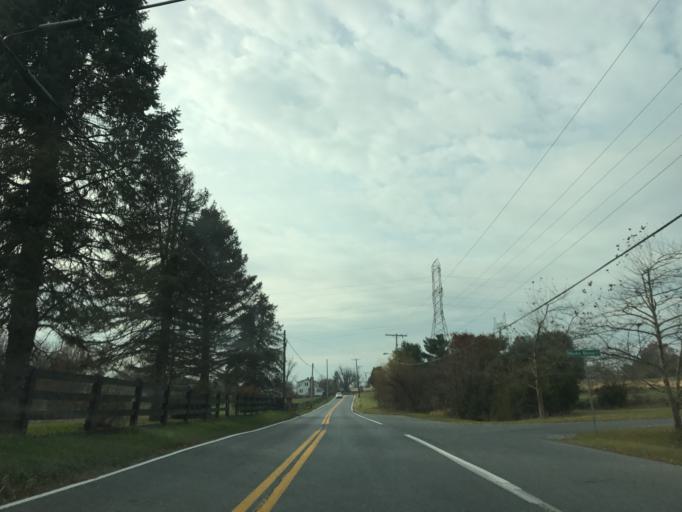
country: US
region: Maryland
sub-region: Baltimore County
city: Randallstown
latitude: 39.3743
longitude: -76.8399
